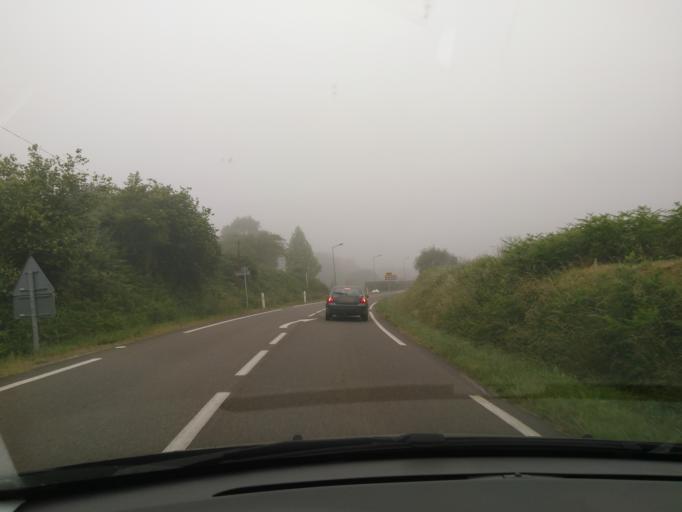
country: FR
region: Aquitaine
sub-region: Departement des Landes
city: Villeneuve-de-Marsan
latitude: 43.8873
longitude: -0.3868
